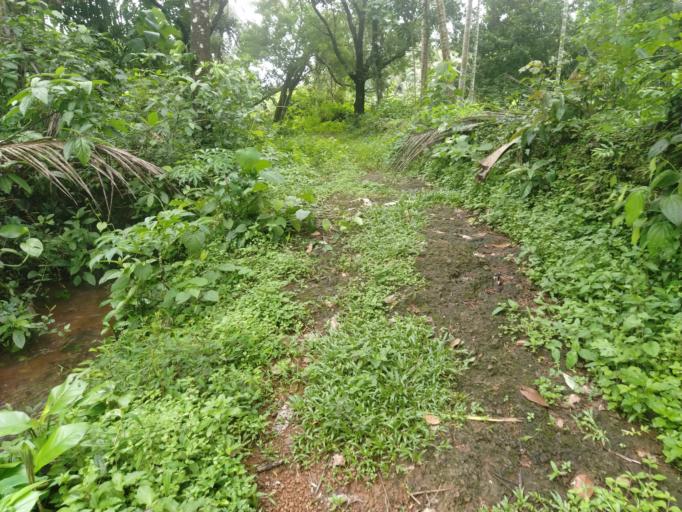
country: IN
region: Kerala
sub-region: Kasaragod District
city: Kannangad
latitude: 12.4048
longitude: 75.0582
